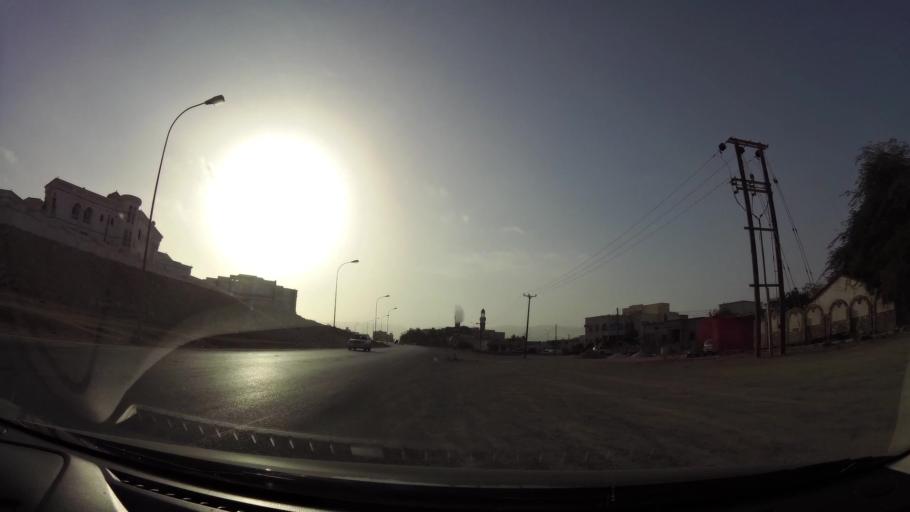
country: OM
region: Zufar
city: Salalah
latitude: 17.0011
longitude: 54.0306
